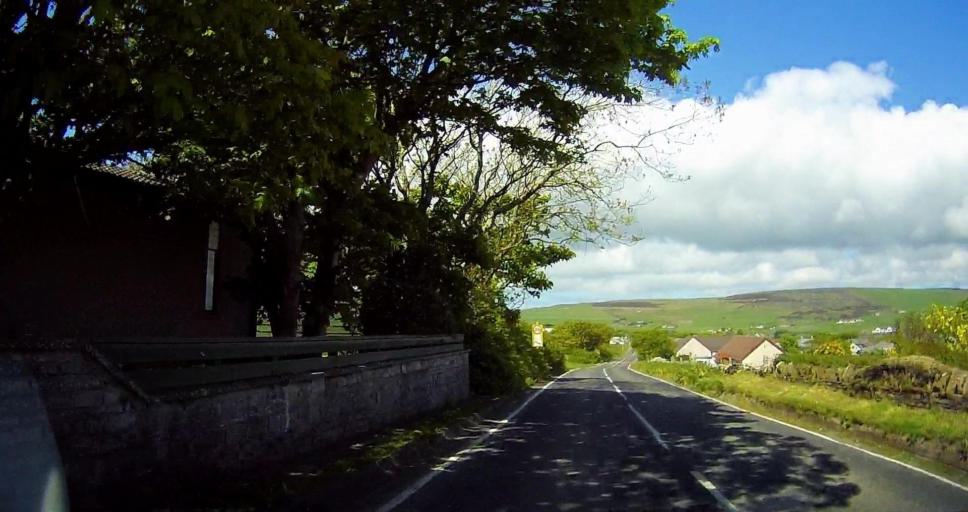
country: GB
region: Scotland
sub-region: Orkney Islands
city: Orkney
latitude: 59.0005
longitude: -3.1038
